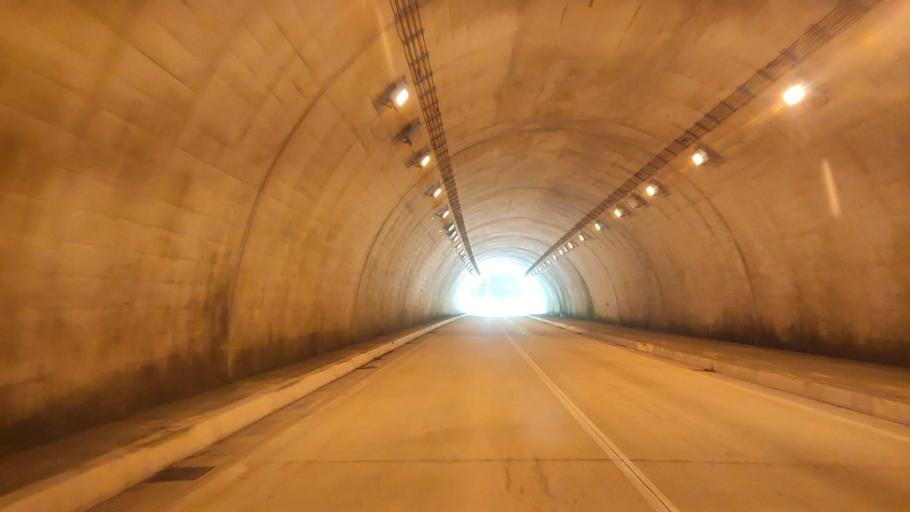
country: JP
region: Ishikawa
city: Komatsu
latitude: 36.3172
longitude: 136.5321
